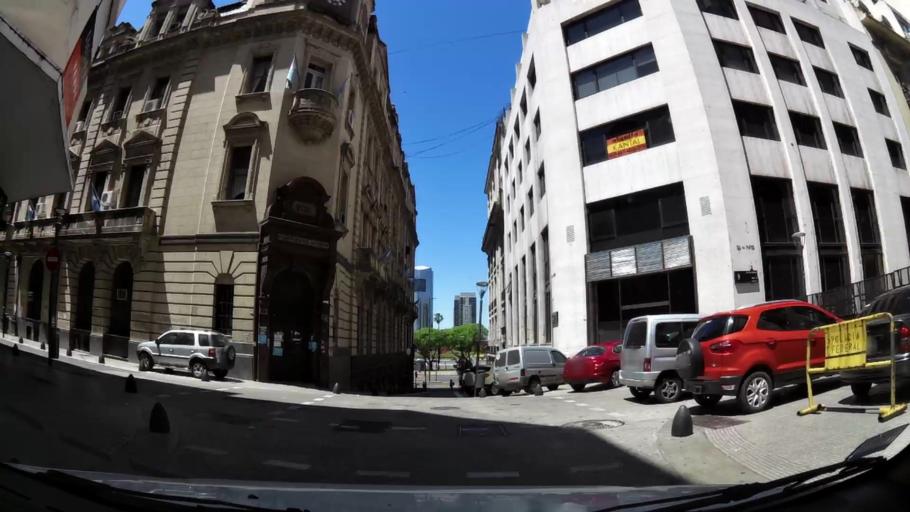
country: AR
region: Buenos Aires F.D.
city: Buenos Aires
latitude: -34.6065
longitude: -58.3711
